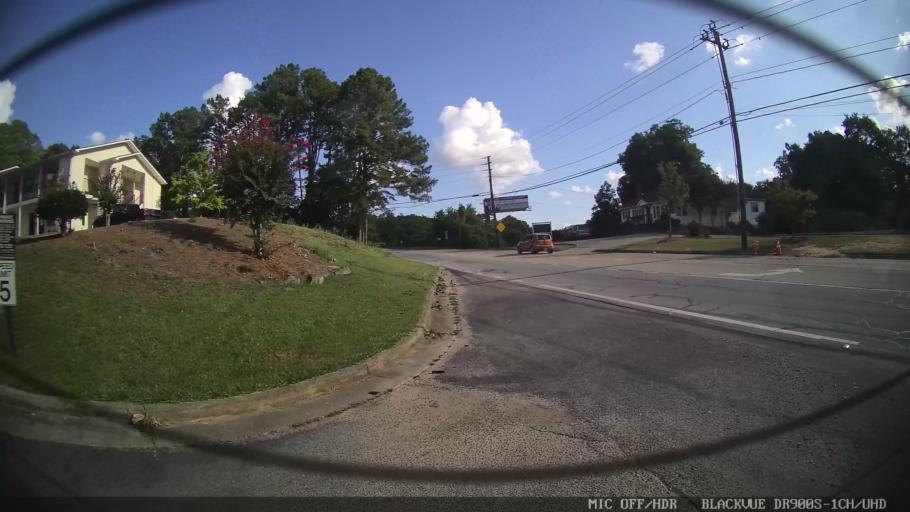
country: US
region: Georgia
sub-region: Floyd County
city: Rome
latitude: 34.2281
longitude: -85.1598
